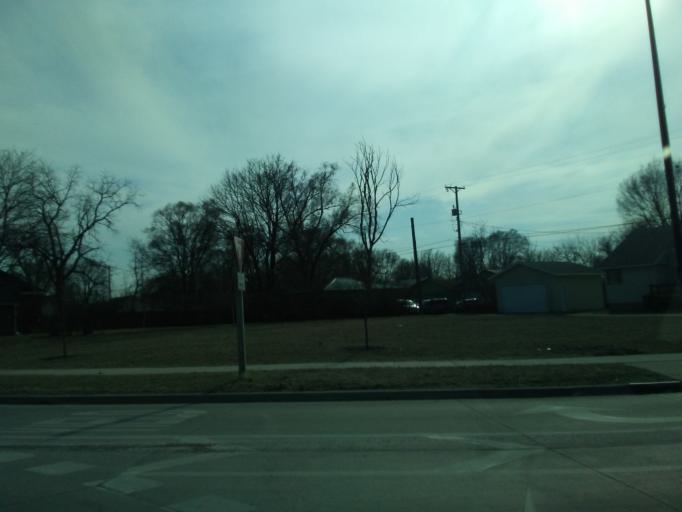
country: US
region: Wisconsin
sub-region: Crawford County
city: Prairie du Chien
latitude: 43.0492
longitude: -91.1412
